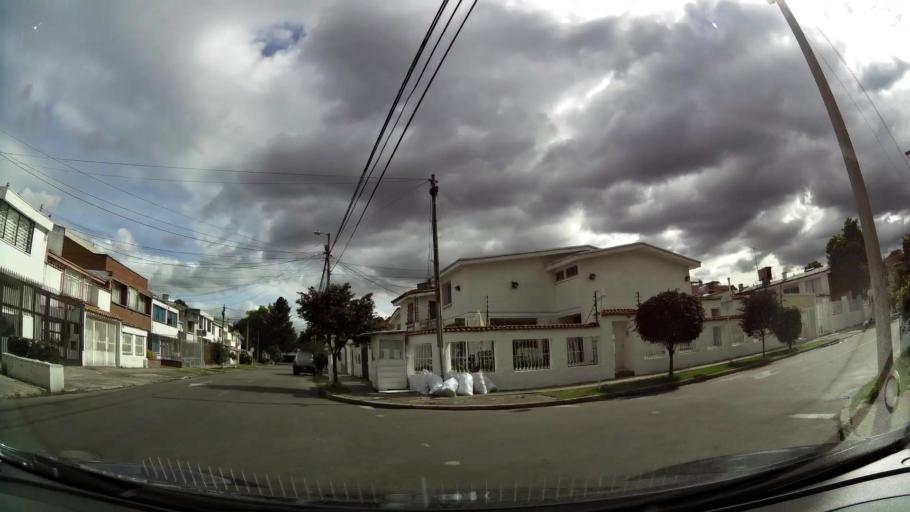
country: CO
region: Bogota D.C.
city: Barrio San Luis
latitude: 4.6912
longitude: -74.0601
